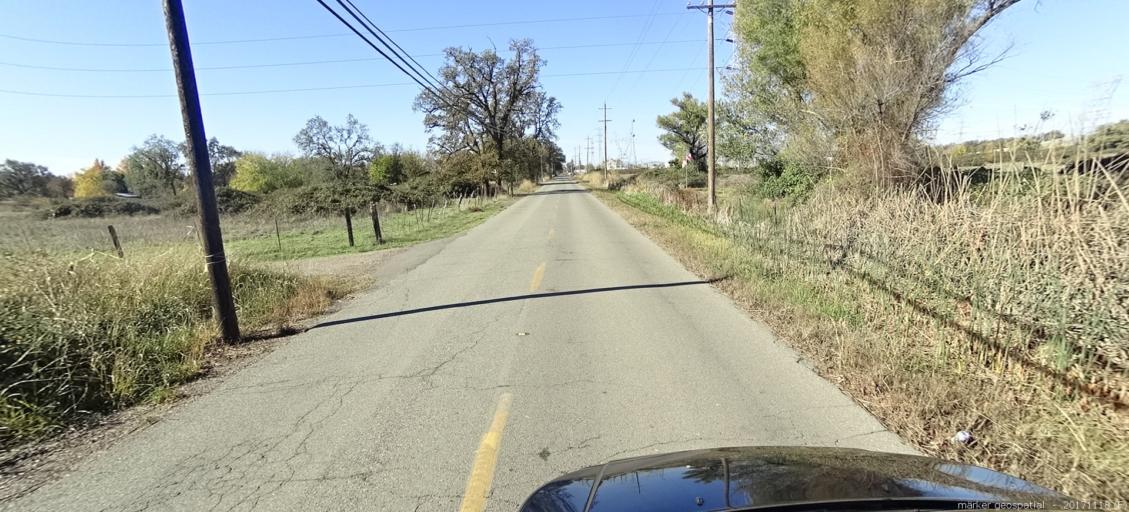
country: US
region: California
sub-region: Shasta County
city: Cottonwood
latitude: 40.3965
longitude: -122.2577
